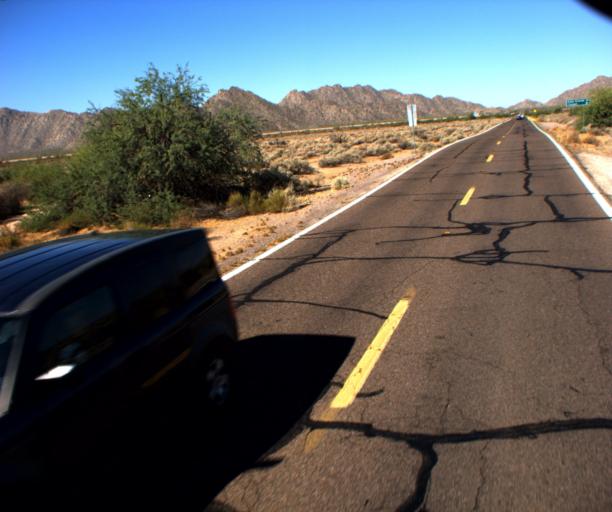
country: US
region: Arizona
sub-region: Pinal County
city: Sacaton
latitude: 33.0577
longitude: -111.6950
